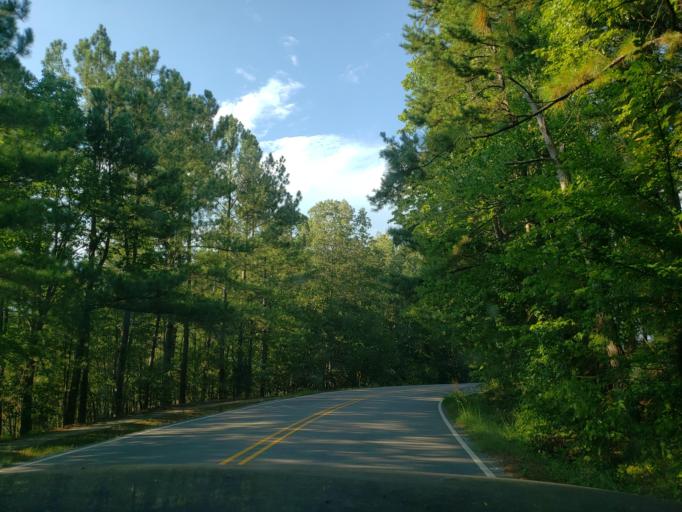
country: US
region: North Carolina
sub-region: Durham County
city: Durham
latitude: 35.9411
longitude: -78.9252
